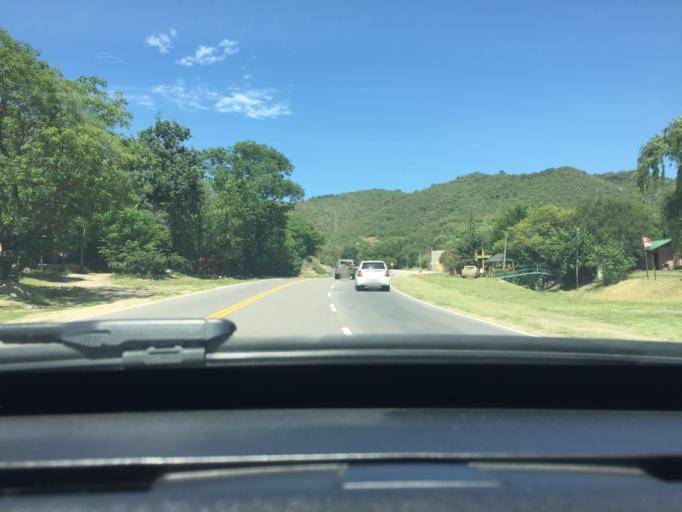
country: AR
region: Cordoba
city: Alta Gracia
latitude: -31.7414
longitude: -64.4600
